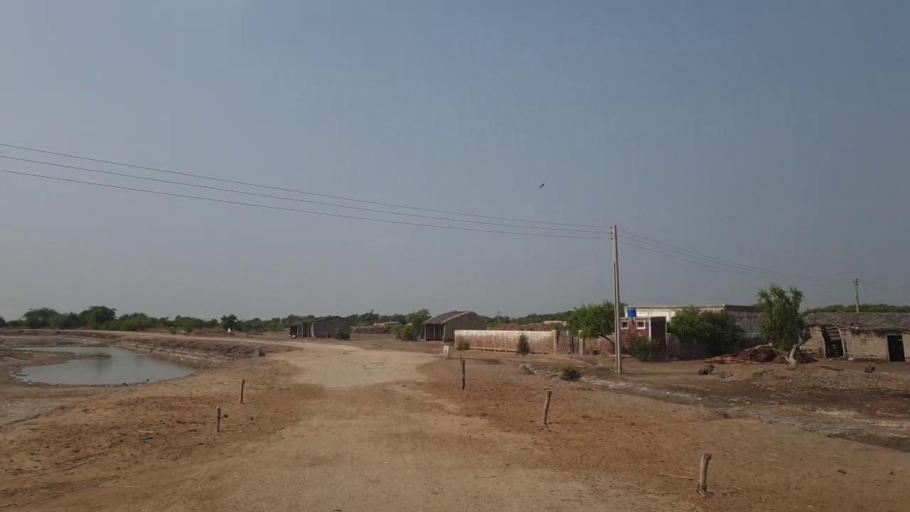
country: PK
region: Sindh
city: Badin
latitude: 24.5457
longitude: 68.6551
